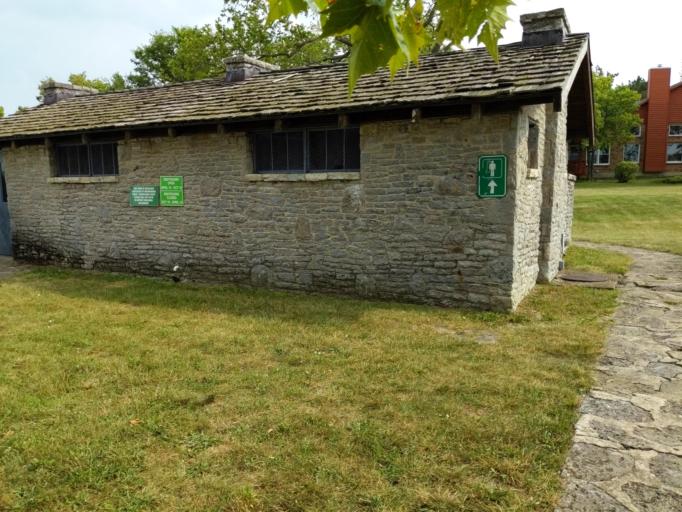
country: US
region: Ohio
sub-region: Montgomery County
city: Miamisburg
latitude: 39.6267
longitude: -84.2795
